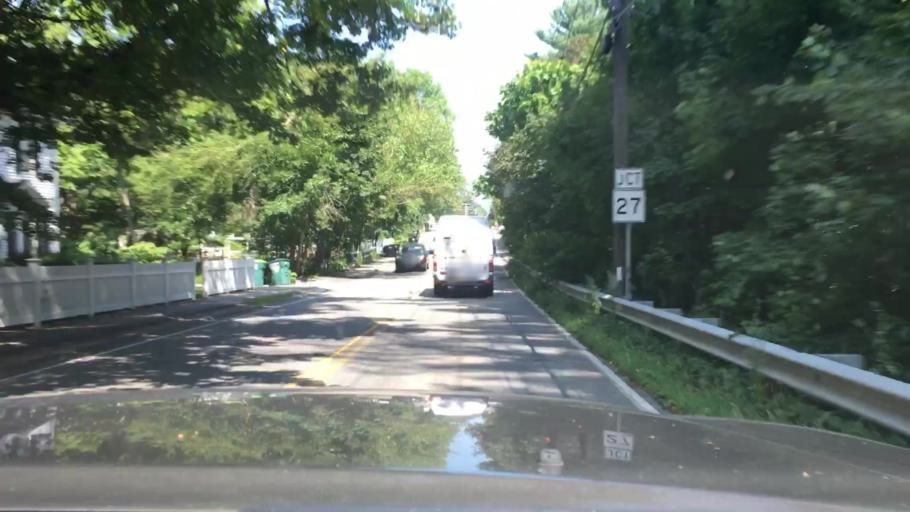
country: US
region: Massachusetts
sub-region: Middlesex County
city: Cochituate
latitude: 42.3157
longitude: -71.3669
